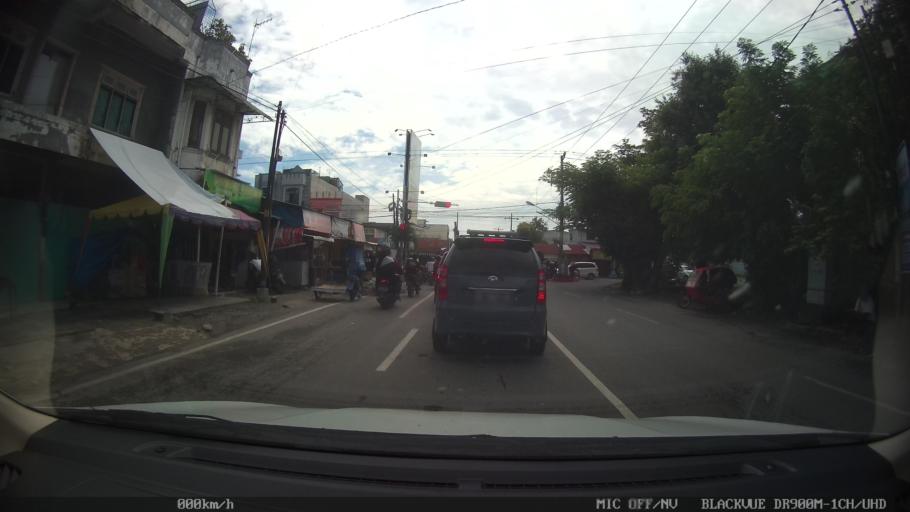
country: ID
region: North Sumatra
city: Medan
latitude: 3.6220
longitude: 98.7071
